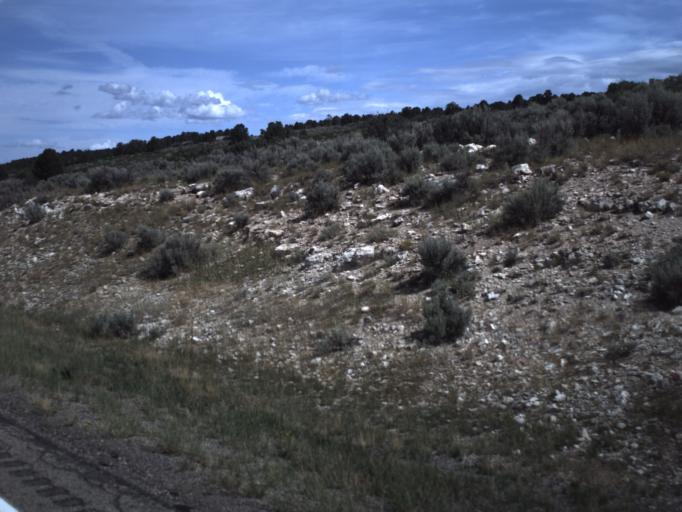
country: US
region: Utah
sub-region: Sanpete County
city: Fairview
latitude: 39.7223
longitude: -111.4725
